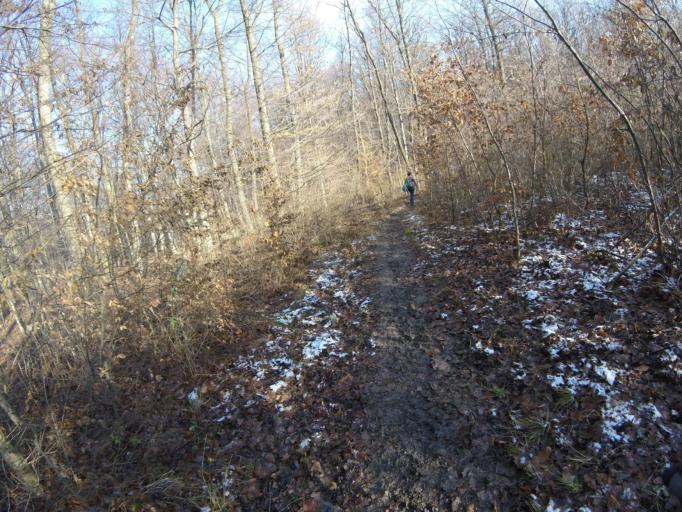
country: HU
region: Komarom-Esztergom
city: Pilismarot
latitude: 47.7528
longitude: 18.8912
